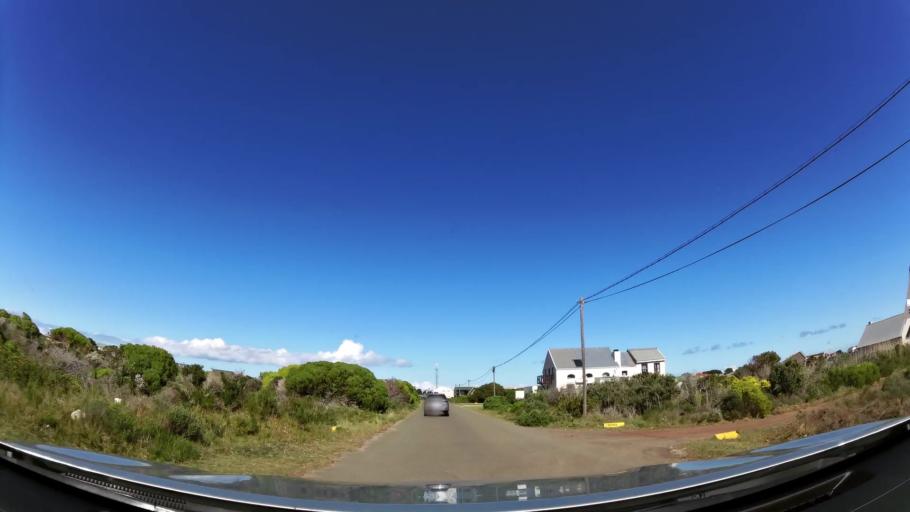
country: ZA
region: Western Cape
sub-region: Overberg District Municipality
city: Grabouw
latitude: -34.3679
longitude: 18.8911
